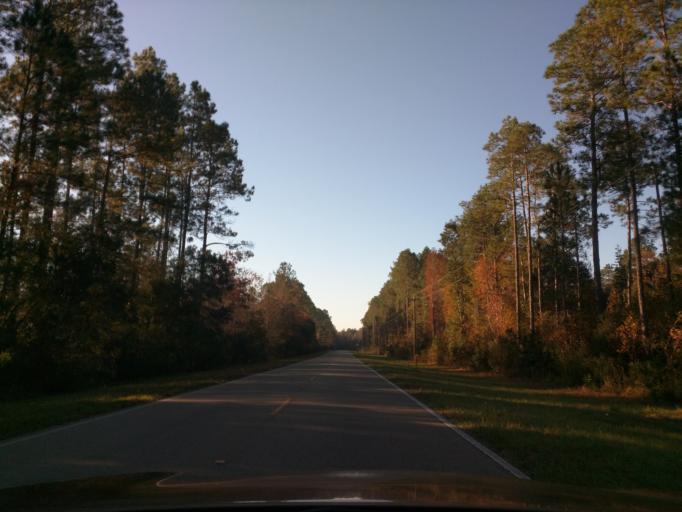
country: US
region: Florida
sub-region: Leon County
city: Woodville
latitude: 30.3331
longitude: -84.1447
